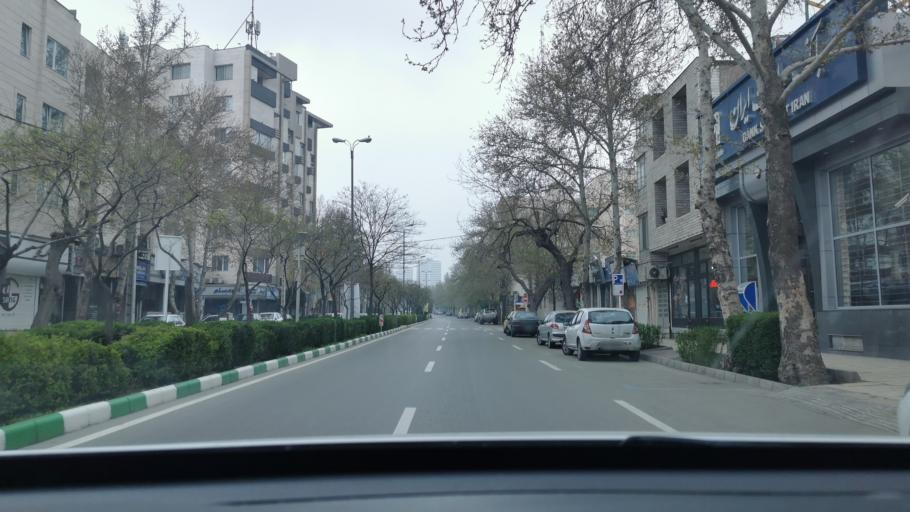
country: IR
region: Razavi Khorasan
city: Mashhad
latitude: 36.2961
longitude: 59.5659
